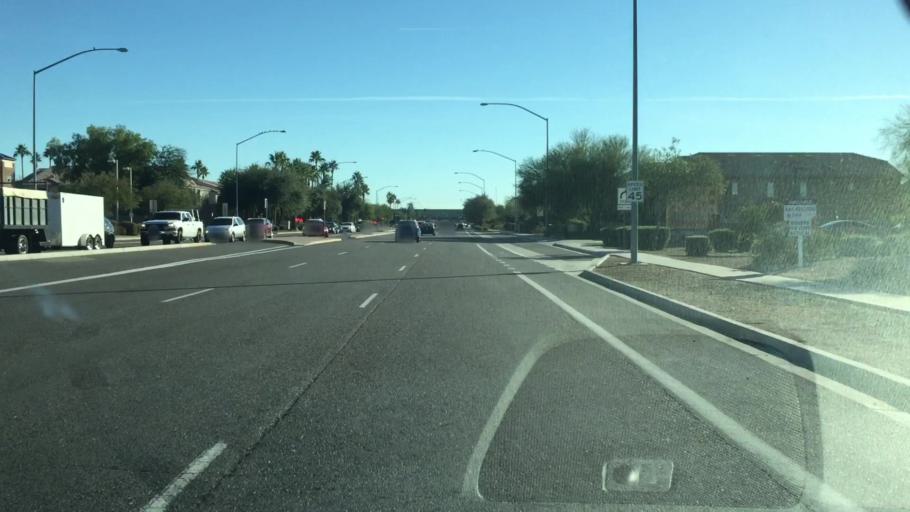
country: US
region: Arizona
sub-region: Maricopa County
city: Gilbert
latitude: 33.3927
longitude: -111.7367
